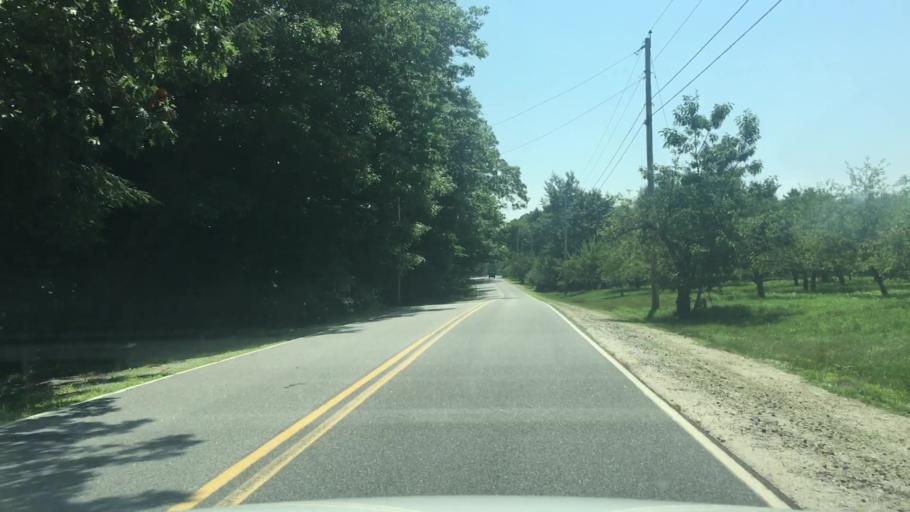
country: US
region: Maine
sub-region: Cumberland County
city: Cumberland Center
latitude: 43.8358
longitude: -70.3050
